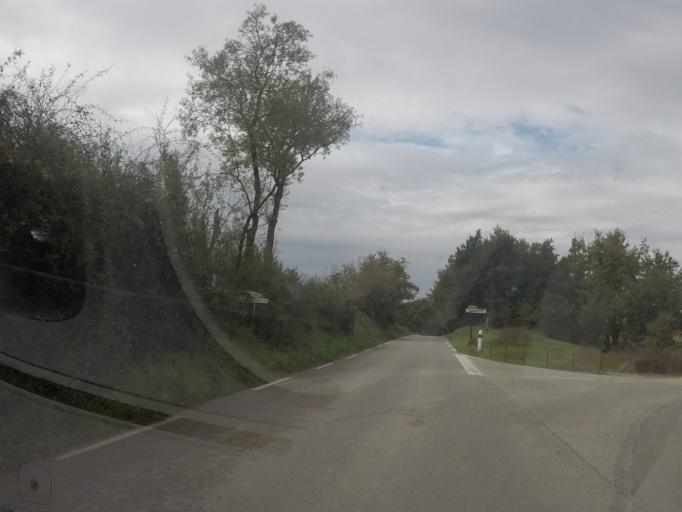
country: FR
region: Provence-Alpes-Cote d'Azur
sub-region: Departement du Vaucluse
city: Ansouis
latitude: 43.7414
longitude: 5.4575
